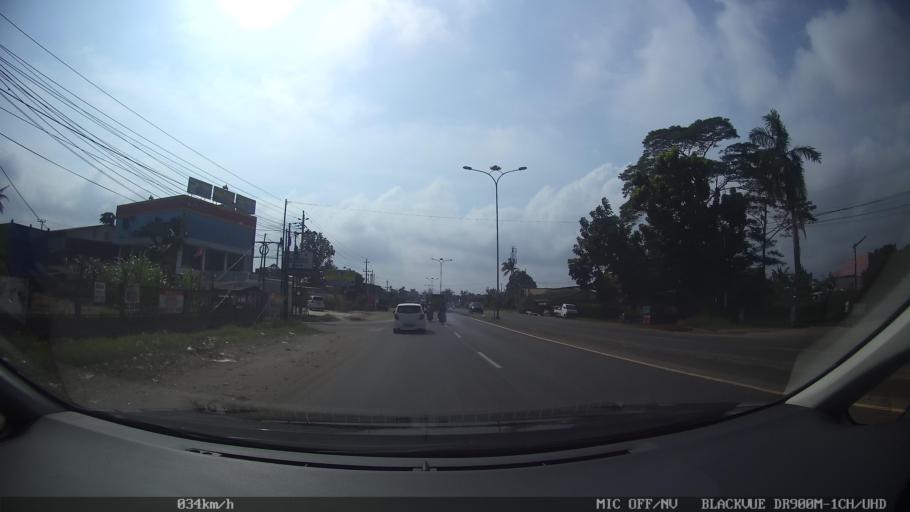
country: ID
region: Lampung
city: Kedaton
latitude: -5.3656
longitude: 105.2657
